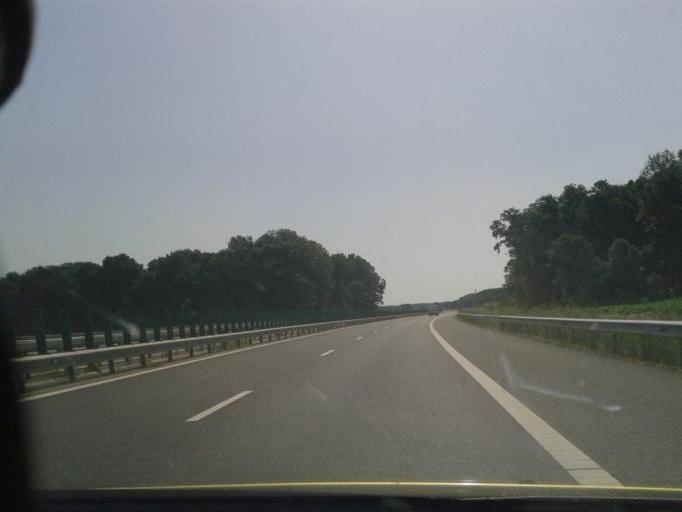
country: RO
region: Prahova
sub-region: Comuna Rafov
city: Rafov
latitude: 44.8885
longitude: 26.1207
